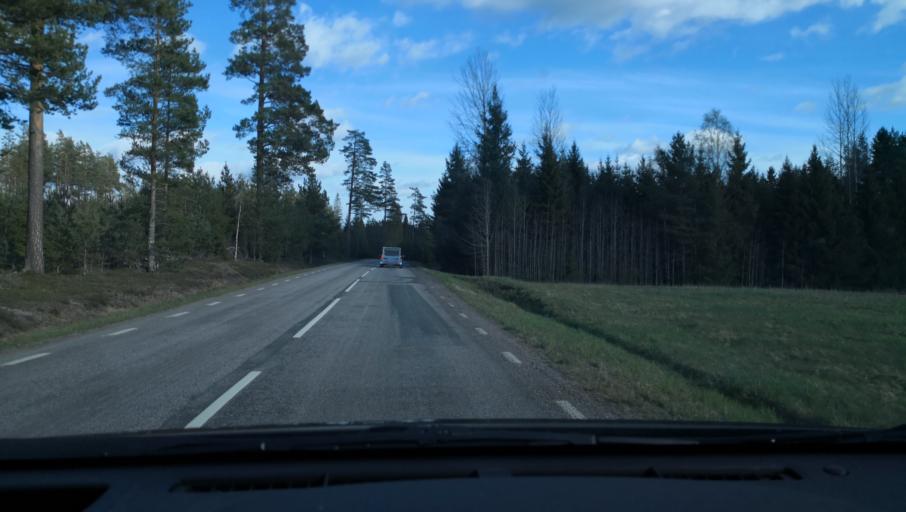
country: SE
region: OErebro
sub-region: Askersunds Kommun
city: Asbro
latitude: 58.9059
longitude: 15.0966
